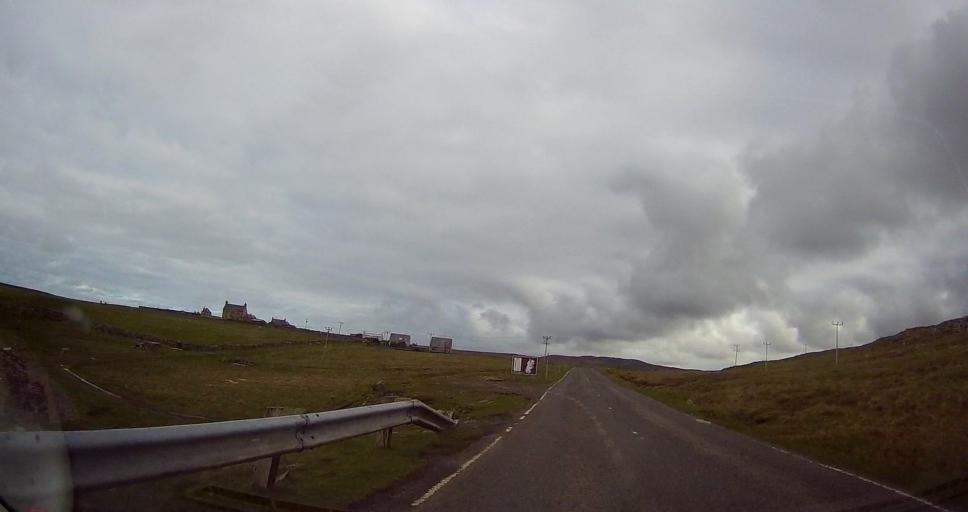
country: GB
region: Scotland
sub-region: Shetland Islands
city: Shetland
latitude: 60.6840
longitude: -0.9658
